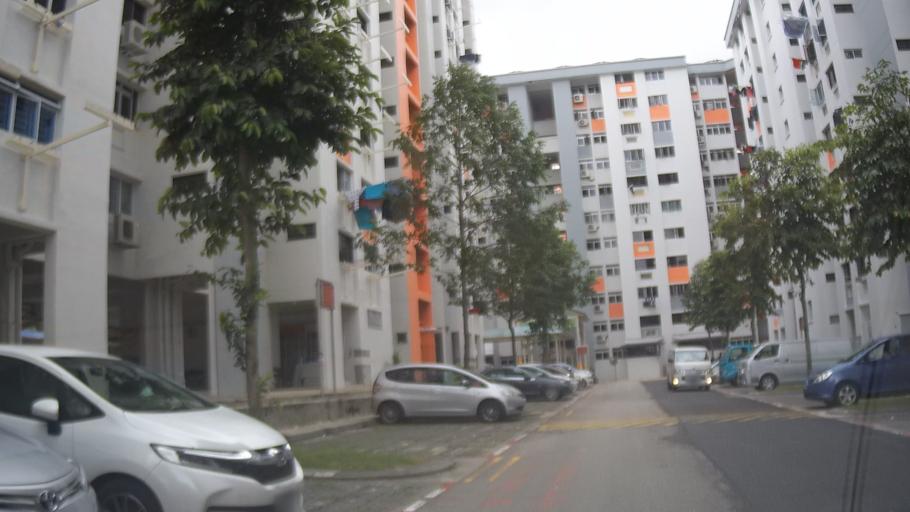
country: MY
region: Johor
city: Johor Bahru
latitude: 1.4322
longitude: 103.7805
